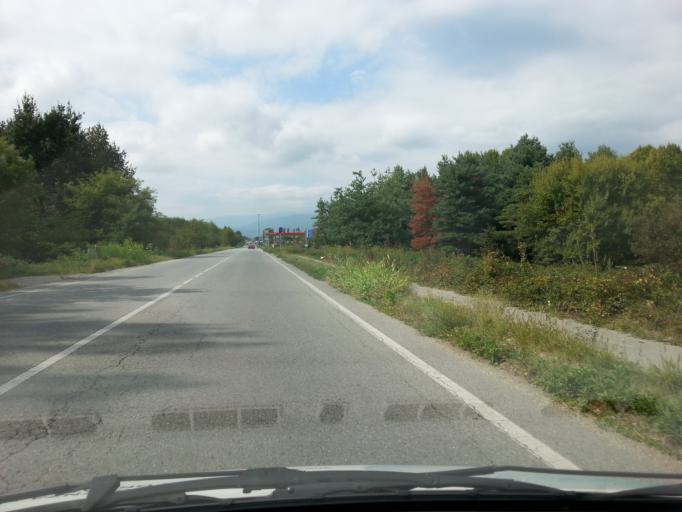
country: IT
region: Piedmont
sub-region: Provincia di Torino
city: Piossasco
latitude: 44.9699
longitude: 7.4344
